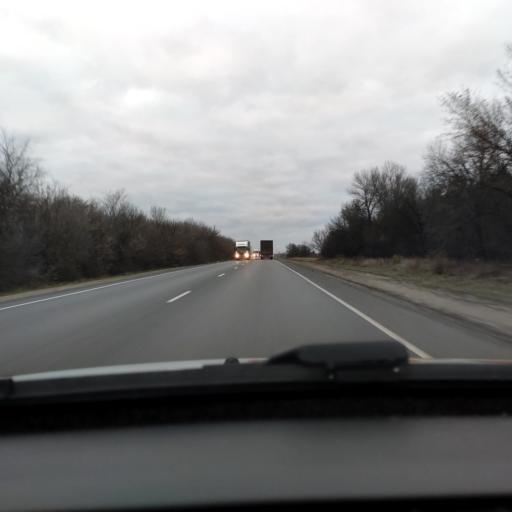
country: RU
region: Lipetsk
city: Khlevnoye
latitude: 52.2501
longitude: 39.1515
